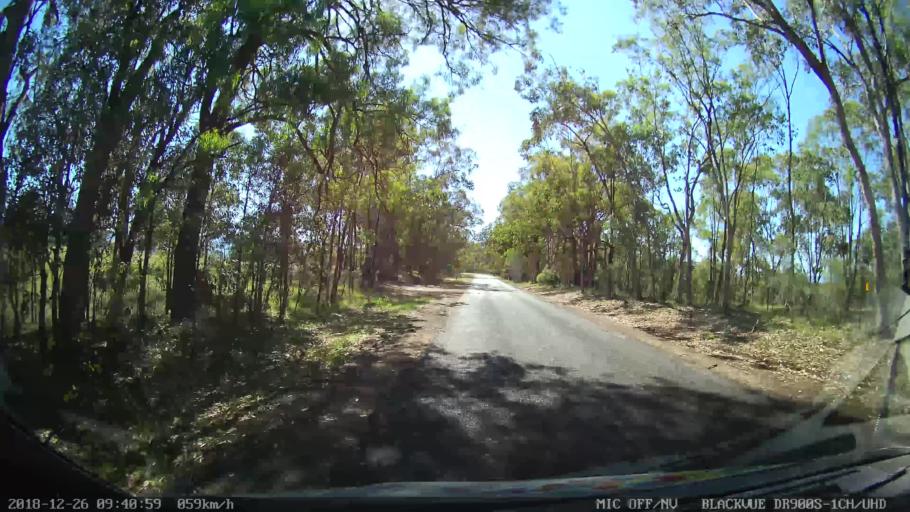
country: AU
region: New South Wales
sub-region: Mid-Western Regional
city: Kandos
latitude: -32.9494
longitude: 150.0679
